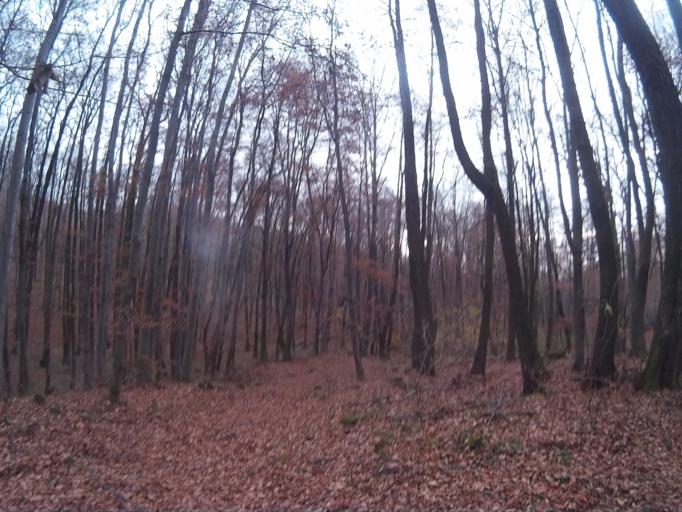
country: HU
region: Veszprem
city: Tapolca
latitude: 46.9520
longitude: 17.4972
